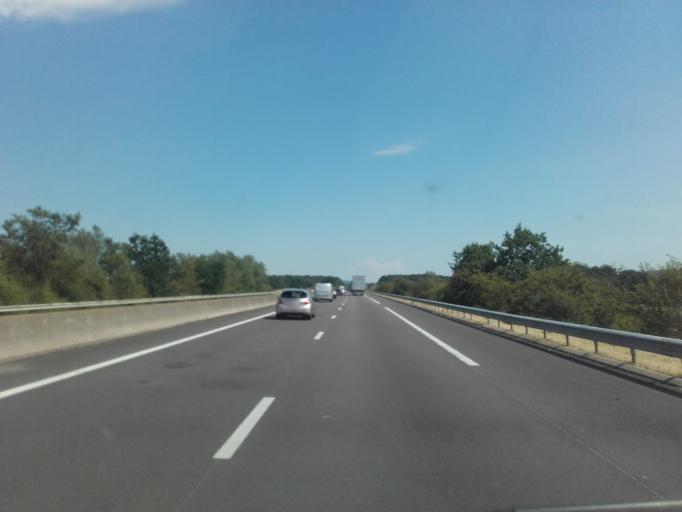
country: FR
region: Bourgogne
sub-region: Departement de la Cote-d'Or
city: Semur-en-Auxois
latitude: 47.3714
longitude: 4.3984
